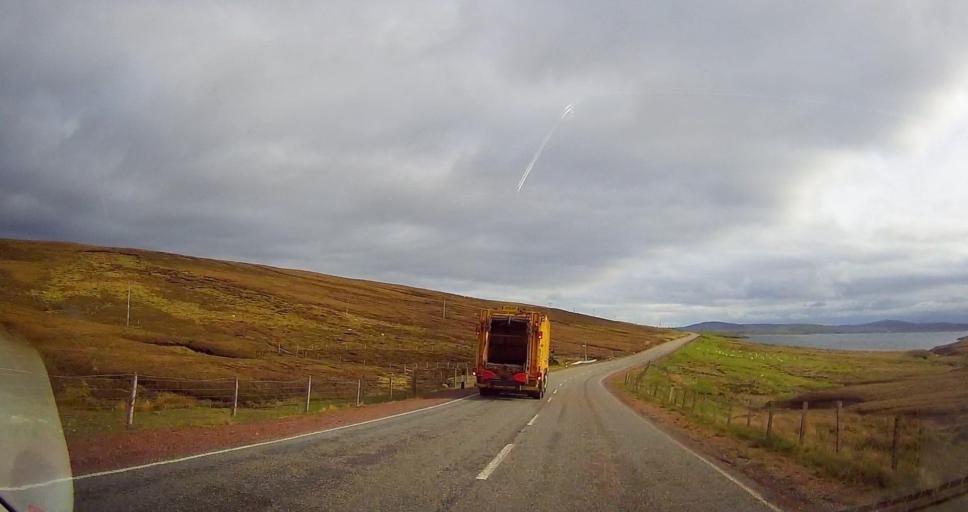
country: GB
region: Scotland
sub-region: Shetland Islands
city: Lerwick
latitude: 60.4519
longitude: -1.2119
